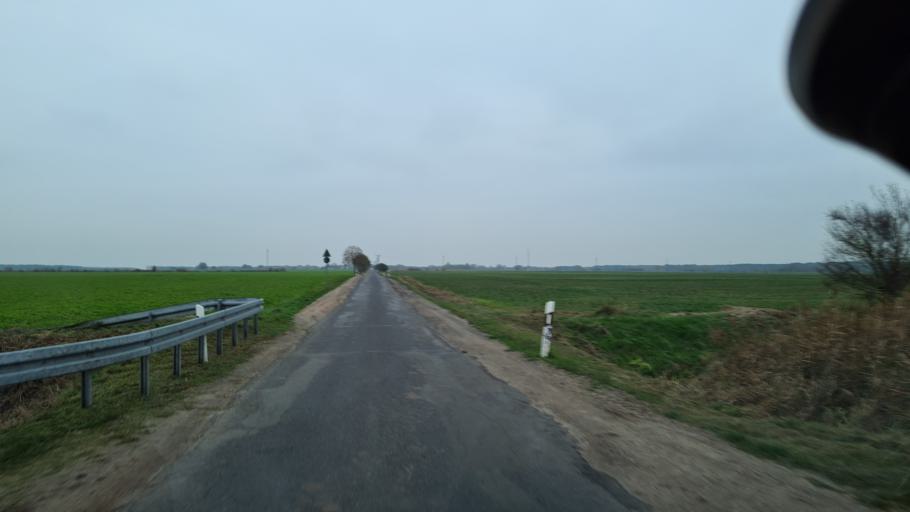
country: DE
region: Brandenburg
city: Ruthnick
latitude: 52.9194
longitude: 12.9919
